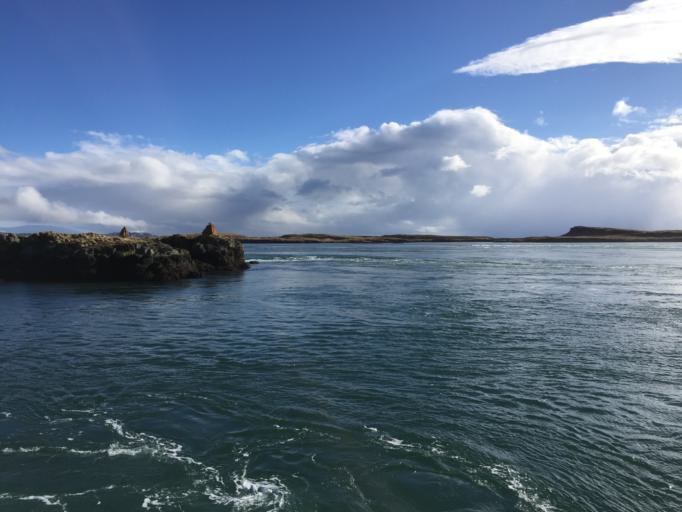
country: IS
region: West
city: Stykkisholmur
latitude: 65.1221
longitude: -22.4910
